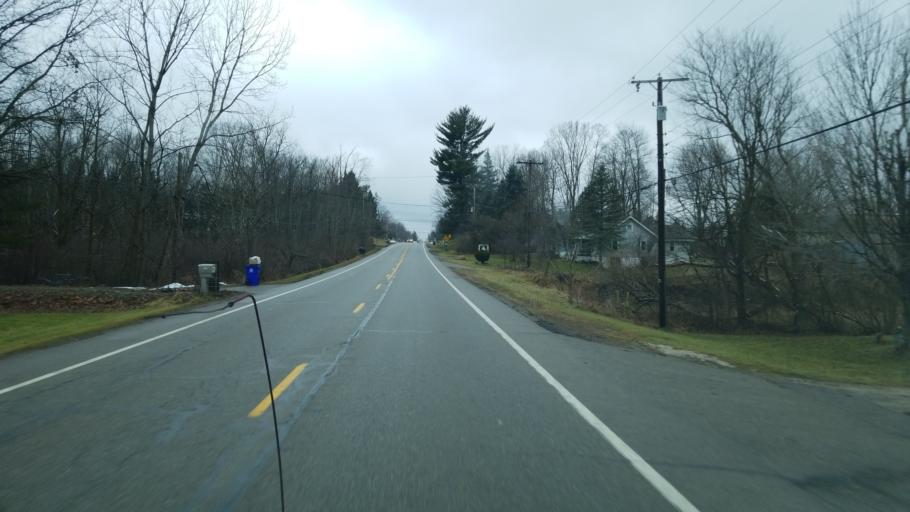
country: US
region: Ohio
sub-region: Portage County
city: Streetsboro
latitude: 41.2399
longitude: -81.3841
